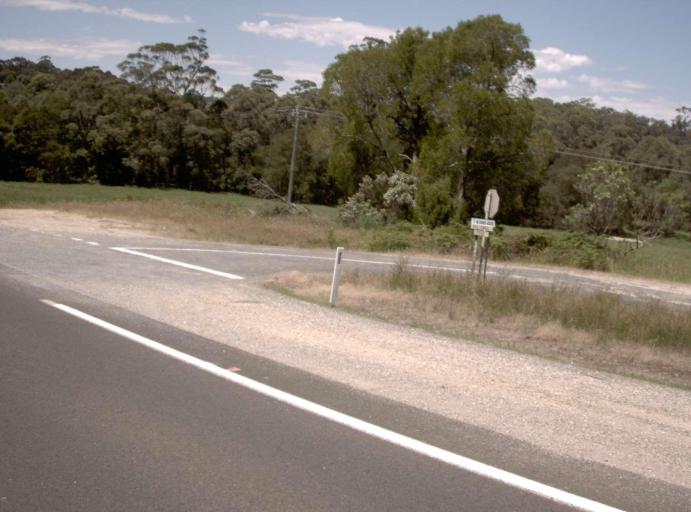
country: AU
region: Victoria
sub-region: East Gippsland
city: Lakes Entrance
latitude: -37.7025
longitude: 148.7145
